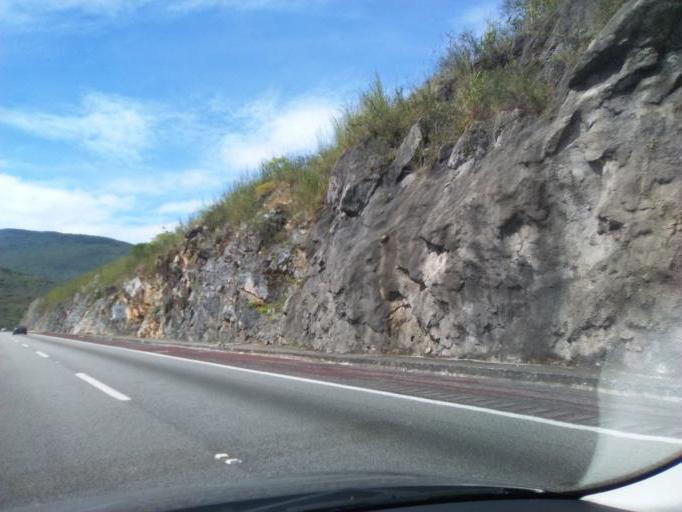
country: MX
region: Guerrero
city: Mazatlan
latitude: 17.4273
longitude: -99.4709
